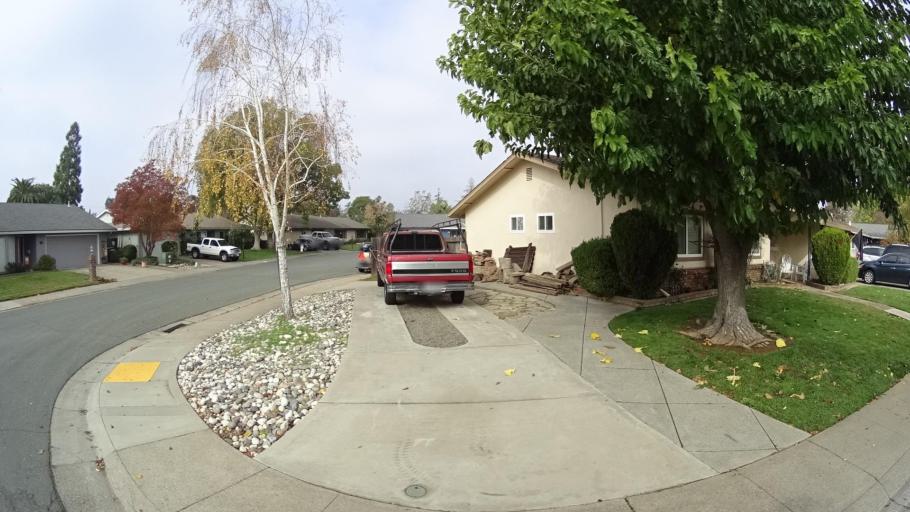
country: US
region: California
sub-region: Sacramento County
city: Elk Grove
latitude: 38.4067
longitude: -121.3655
